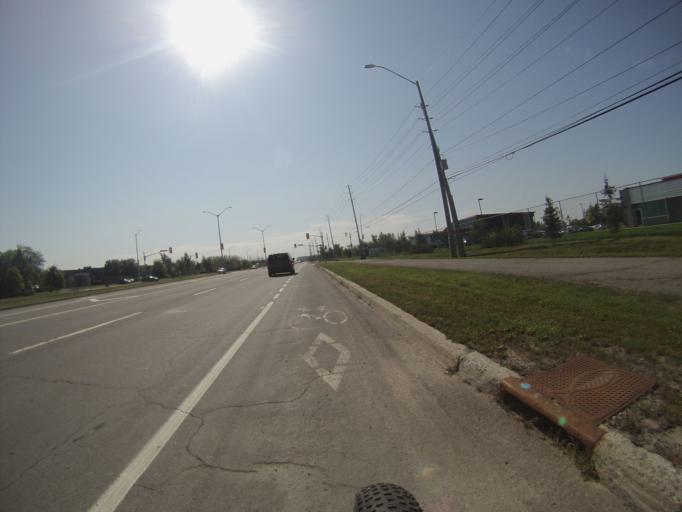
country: CA
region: Ontario
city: Ottawa
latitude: 45.3783
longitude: -75.6271
